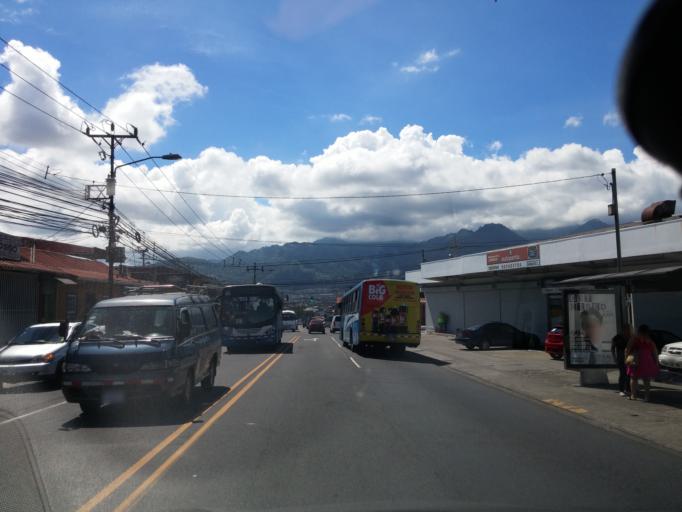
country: CR
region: San Jose
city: San Jose
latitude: 9.9245
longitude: -84.0918
